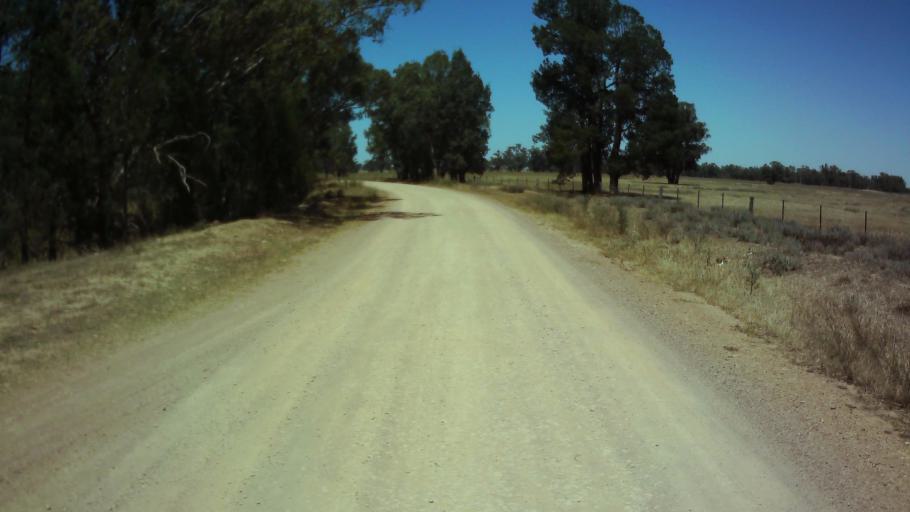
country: AU
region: New South Wales
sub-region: Weddin
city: Grenfell
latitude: -34.0287
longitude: 148.0154
